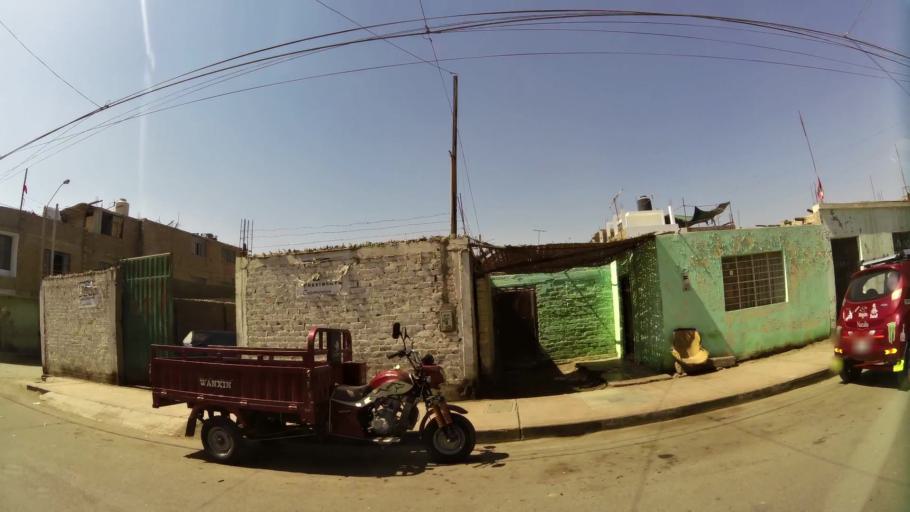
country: PE
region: Ica
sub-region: Provincia de Ica
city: Ica
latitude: -14.0688
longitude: -75.7239
